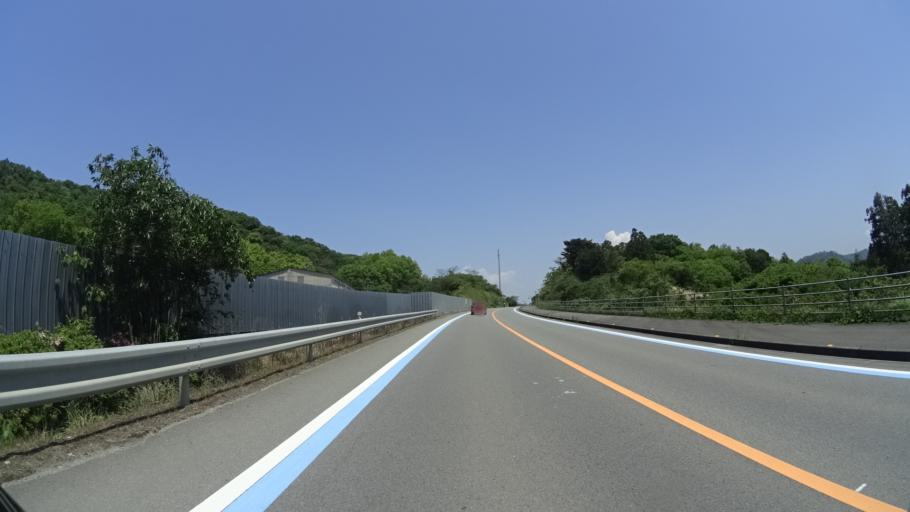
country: JP
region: Ehime
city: Iyo
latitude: 33.7174
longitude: 132.6755
